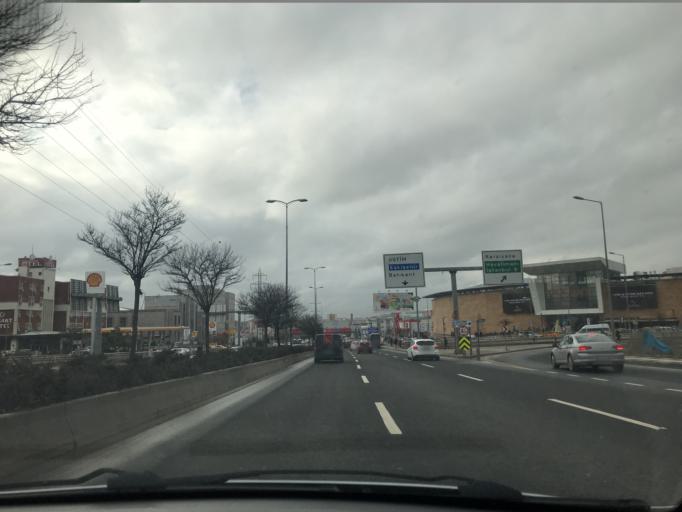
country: TR
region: Ankara
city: Batikent
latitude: 39.9610
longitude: 32.7730
